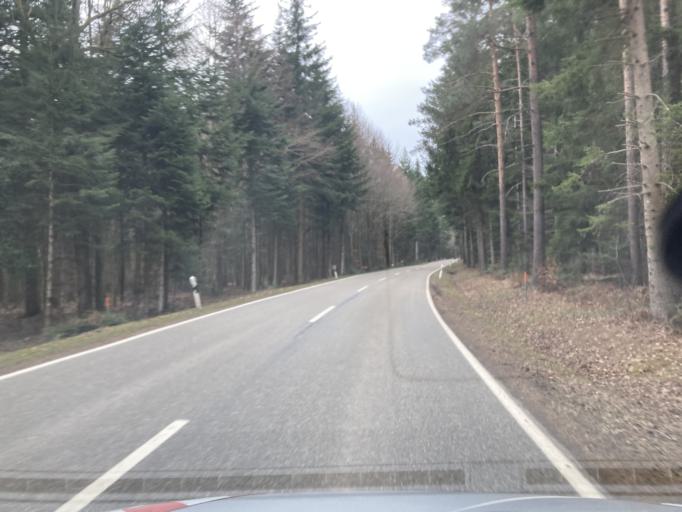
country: DE
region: Baden-Wuerttemberg
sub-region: Karlsruhe Region
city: Neuweiler
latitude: 48.6675
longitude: 8.6214
